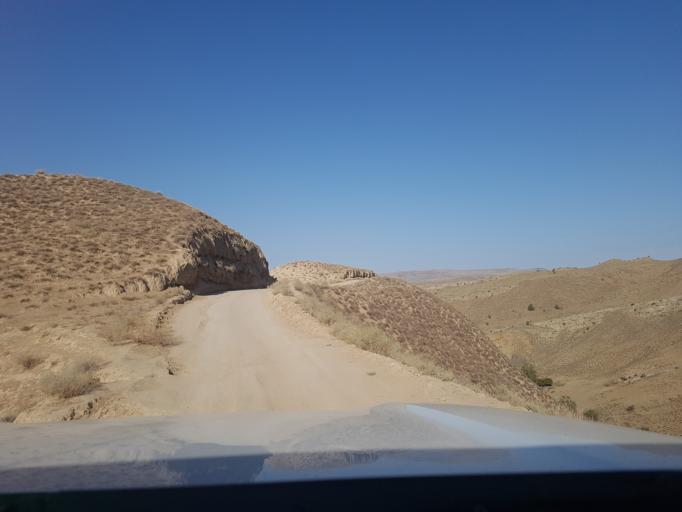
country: TM
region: Balkan
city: Magtymguly
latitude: 38.3032
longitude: 56.7996
